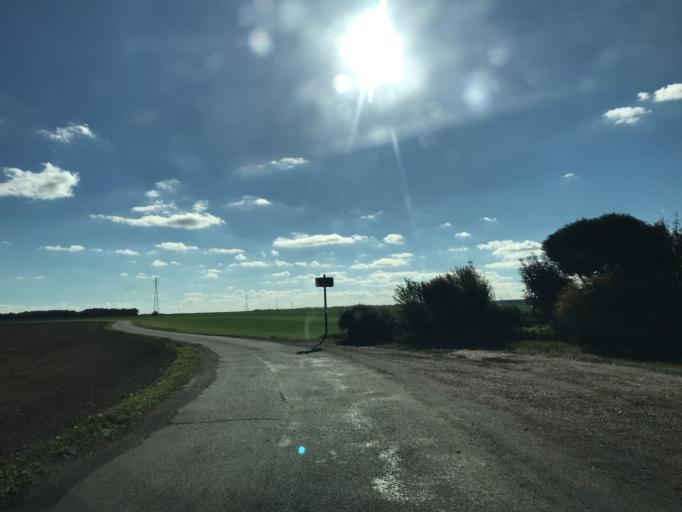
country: FR
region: Haute-Normandie
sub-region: Departement de l'Eure
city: Gravigny
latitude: 49.0817
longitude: 1.2387
